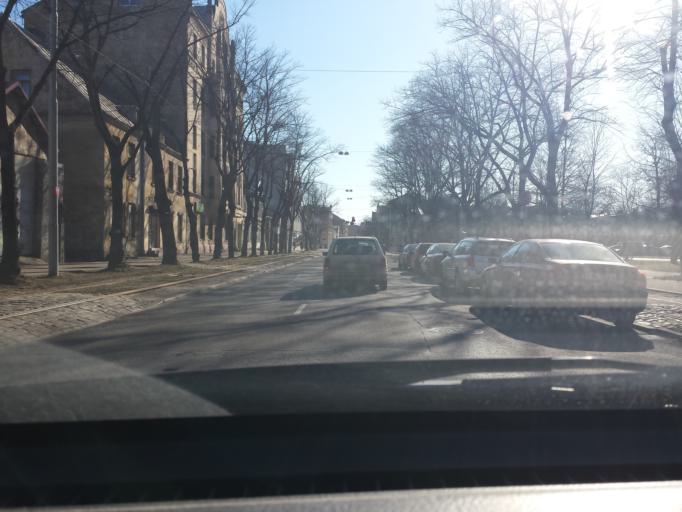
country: LV
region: Riga
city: Riga
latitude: 56.9668
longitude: 24.1343
